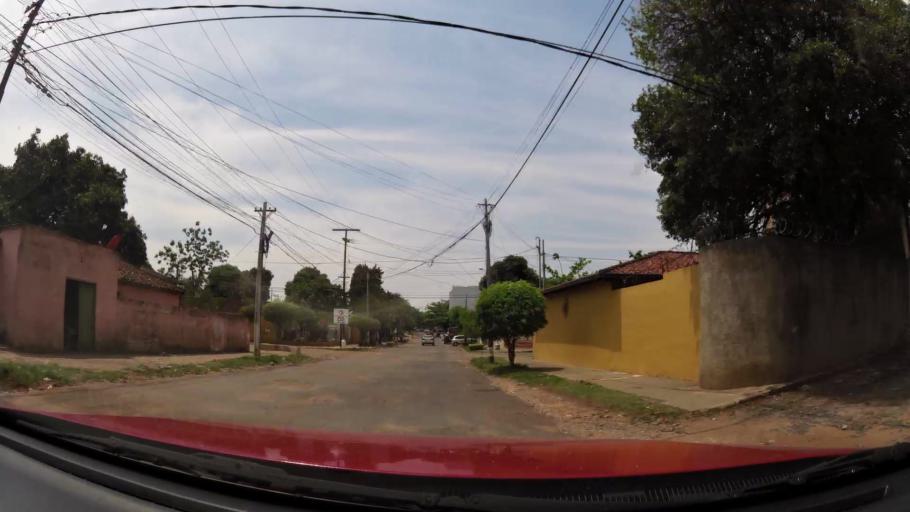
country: PY
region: Central
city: Fernando de la Mora
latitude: -25.3168
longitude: -57.5636
